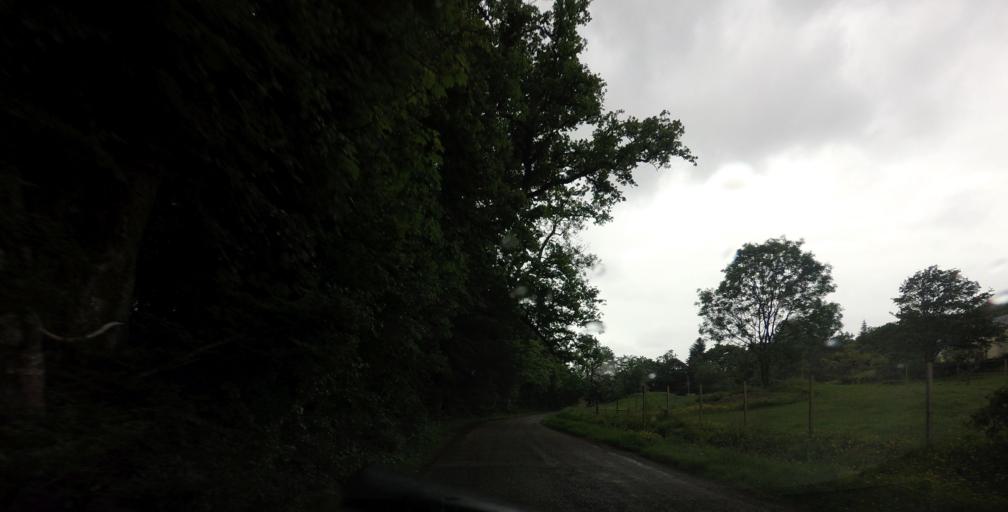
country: GB
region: Scotland
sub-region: Argyll and Bute
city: Oban
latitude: 56.6995
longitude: -5.5708
